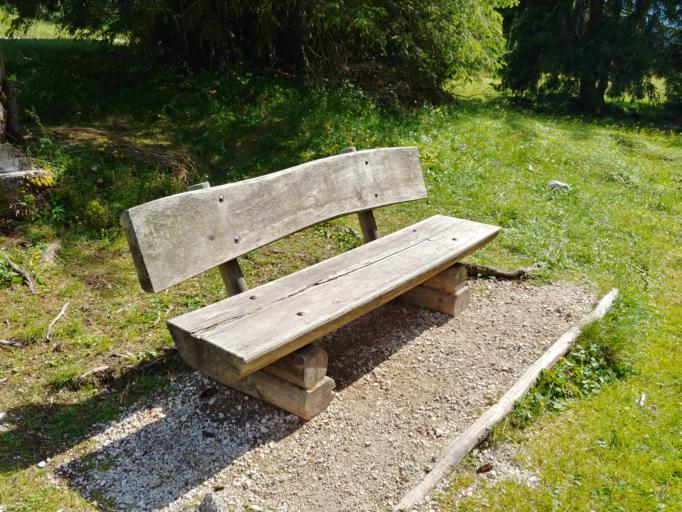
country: IT
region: Trentino-Alto Adige
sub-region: Bolzano
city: Selva
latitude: 46.5721
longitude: 11.7910
